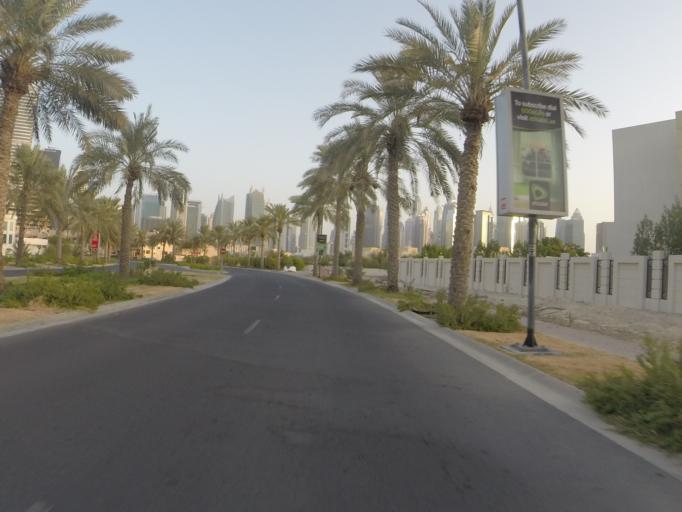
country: AE
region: Dubai
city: Dubai
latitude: 25.0665
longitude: 55.1506
